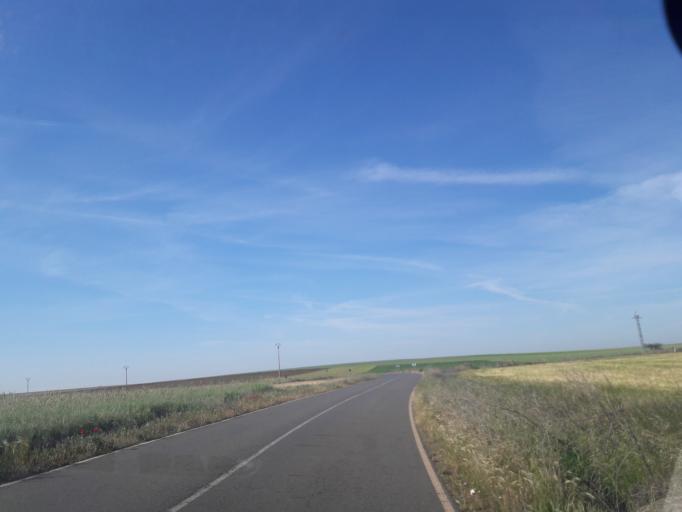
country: ES
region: Castille and Leon
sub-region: Provincia de Salamanca
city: Tardaguila
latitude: 41.1096
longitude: -5.5730
